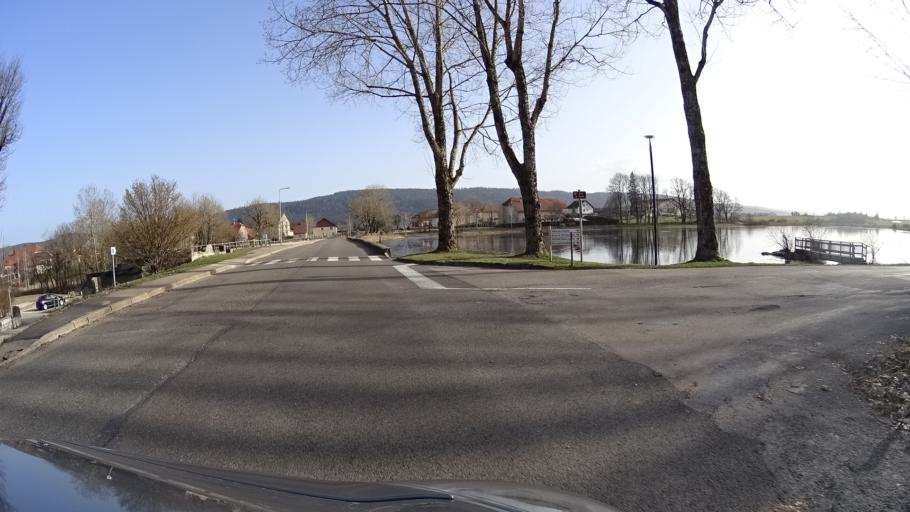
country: FR
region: Franche-Comte
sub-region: Departement du Doubs
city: Frasne
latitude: 46.8668
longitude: 6.2174
